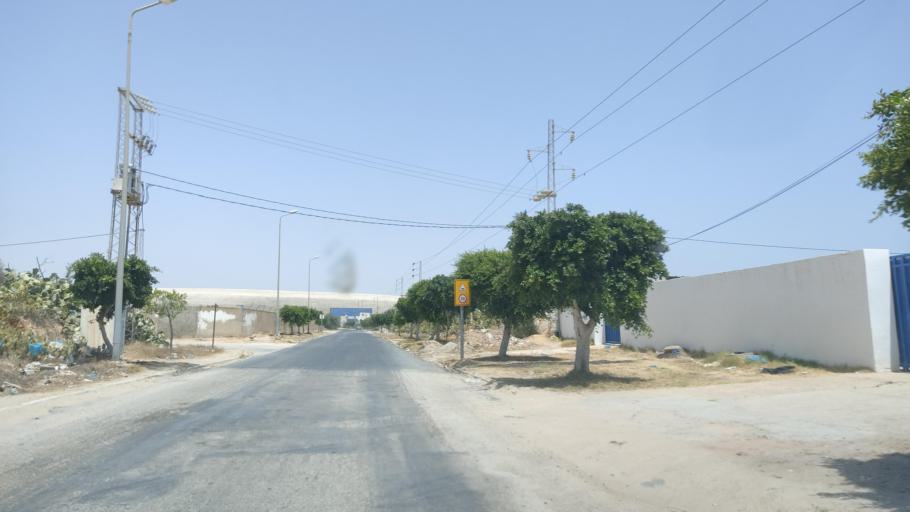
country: TN
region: Safaqis
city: Sfax
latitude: 34.6872
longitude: 10.7245
